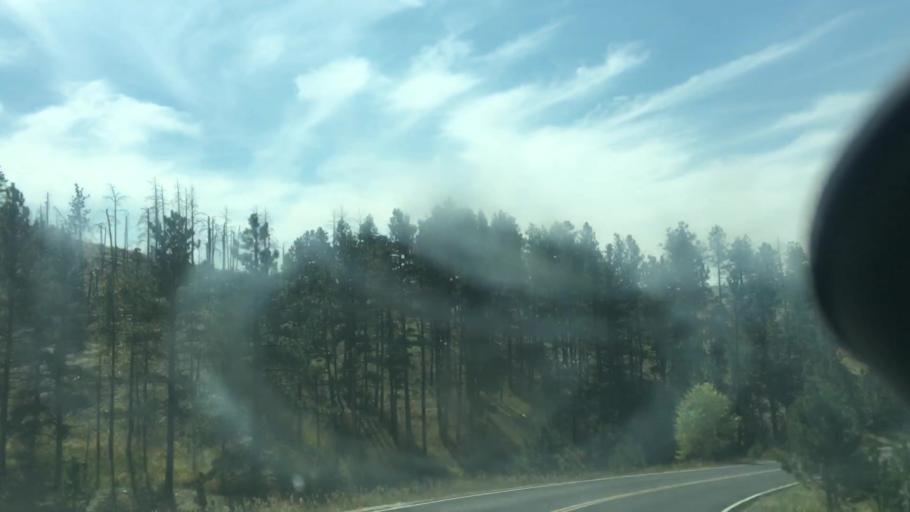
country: US
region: Colorado
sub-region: Larimer County
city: Laporte
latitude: 40.5903
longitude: -105.3363
